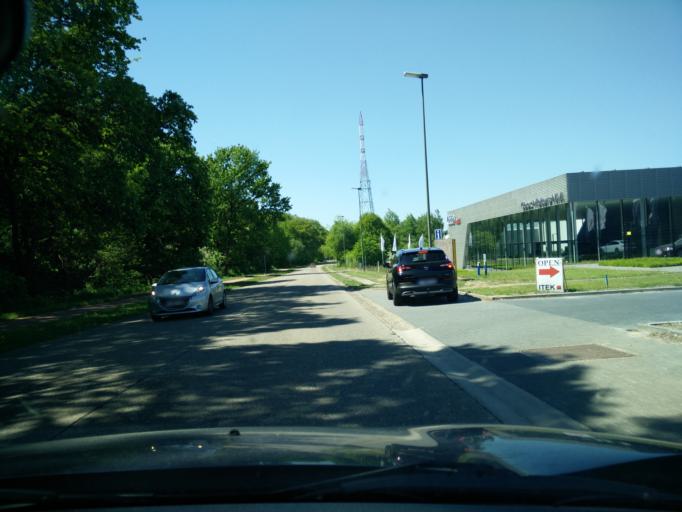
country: BE
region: Flanders
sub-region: Provincie Limburg
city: Maasmechelen
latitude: 51.0074
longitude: 5.7119
